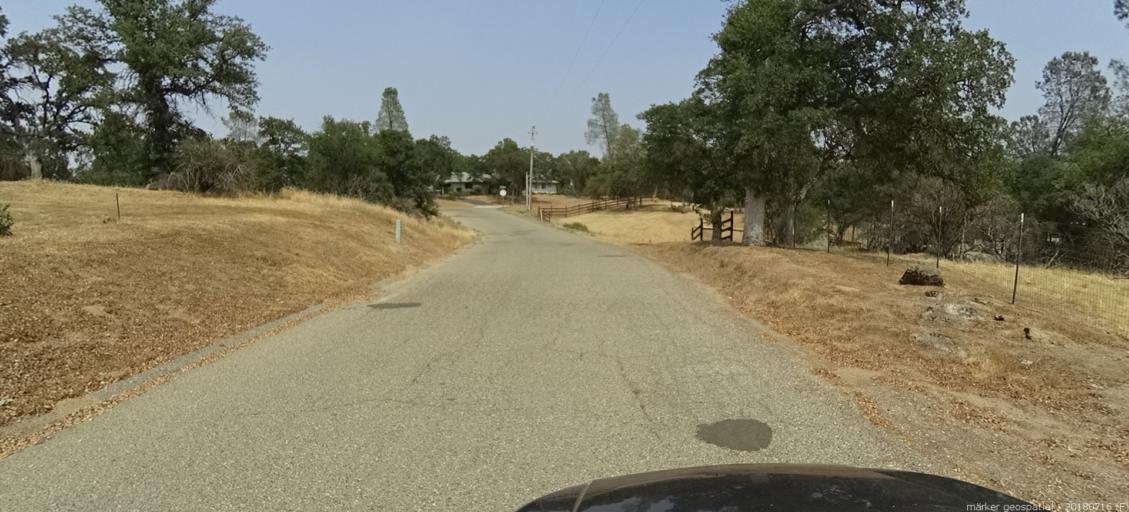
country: US
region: California
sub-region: Madera County
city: Yosemite Lakes
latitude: 37.2161
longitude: -119.7804
